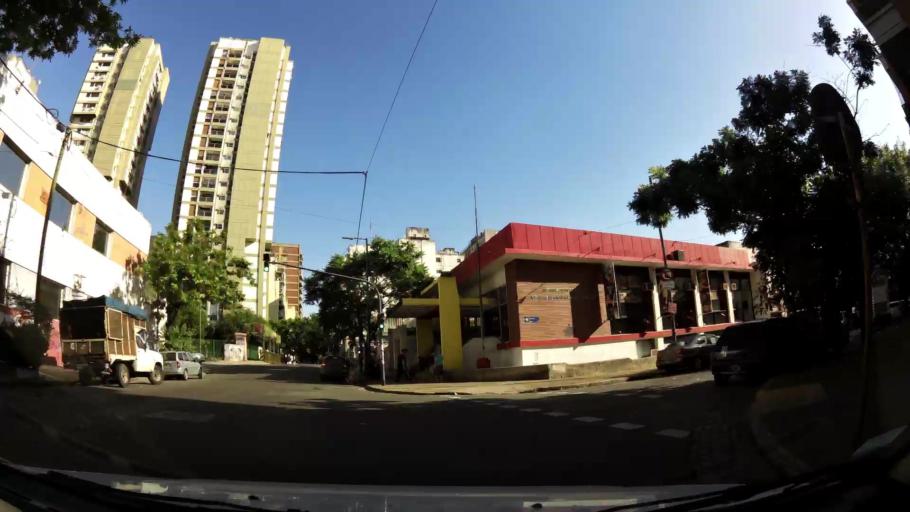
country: AR
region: Buenos Aires F.D.
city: Villa Santa Rita
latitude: -34.6167
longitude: -58.4388
